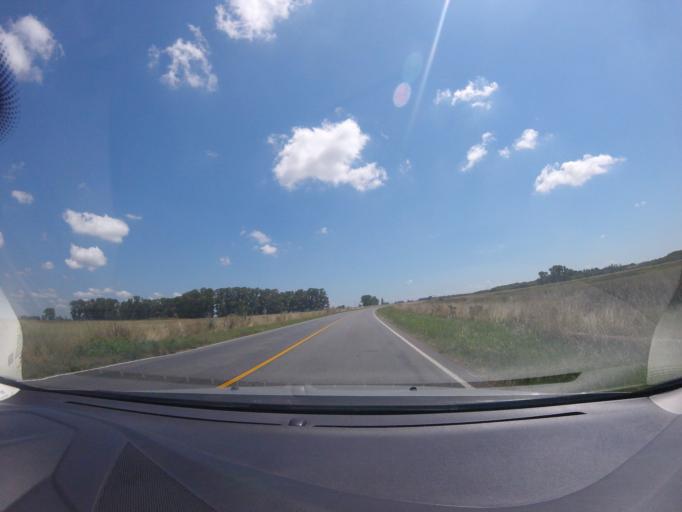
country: AR
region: Buenos Aires
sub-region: Partido de Rauch
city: Rauch
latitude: -36.6960
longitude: -59.0660
